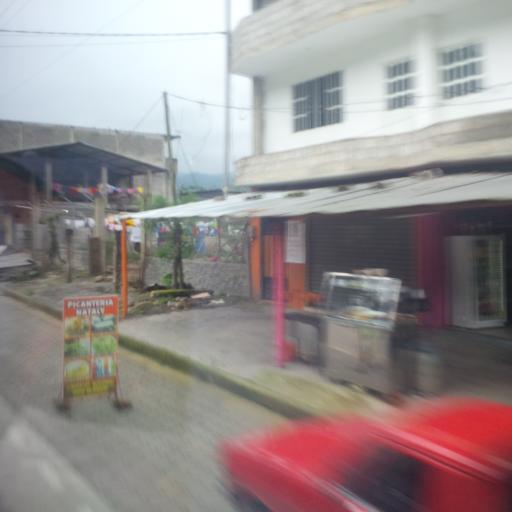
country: EC
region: Chimborazo
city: Alausi
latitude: -2.2003
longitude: -79.1210
